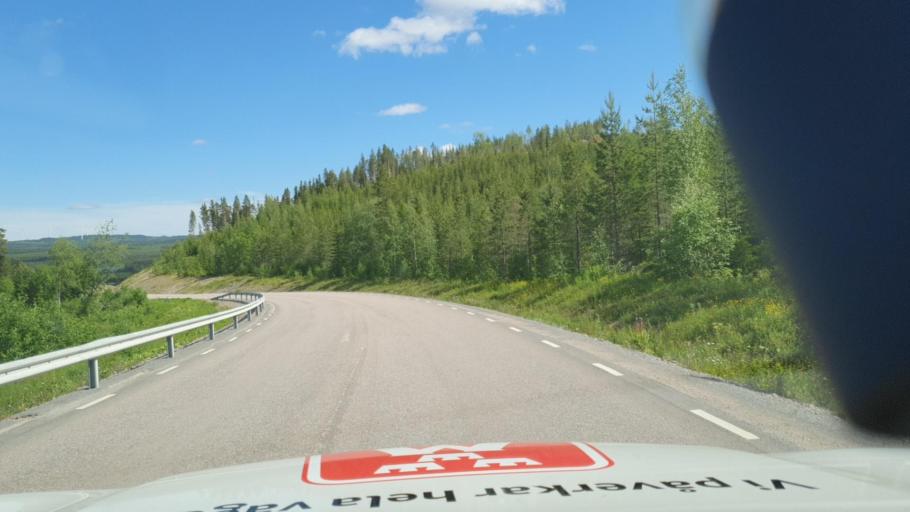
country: SE
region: Jaemtland
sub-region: Bergs Kommun
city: Hoverberg
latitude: 62.4654
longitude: 14.5143
